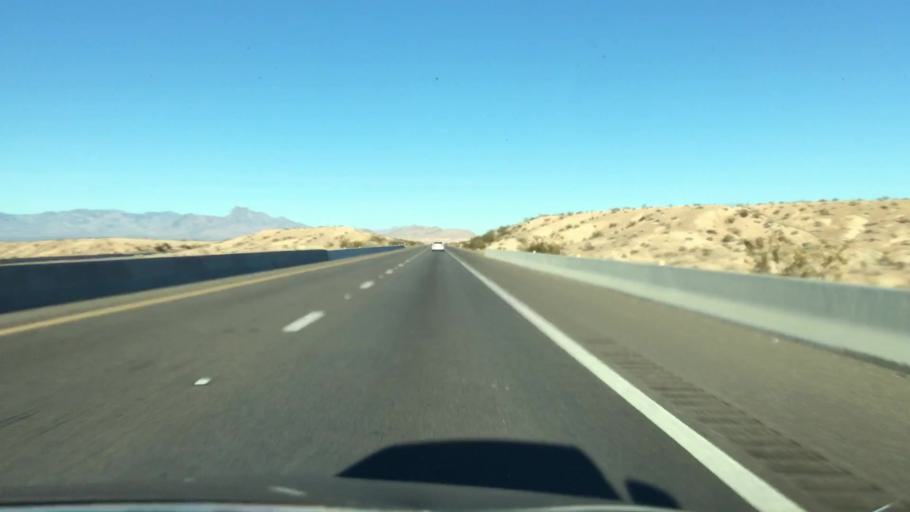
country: US
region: Nevada
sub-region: Clark County
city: Moapa Town
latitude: 36.6082
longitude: -114.6309
